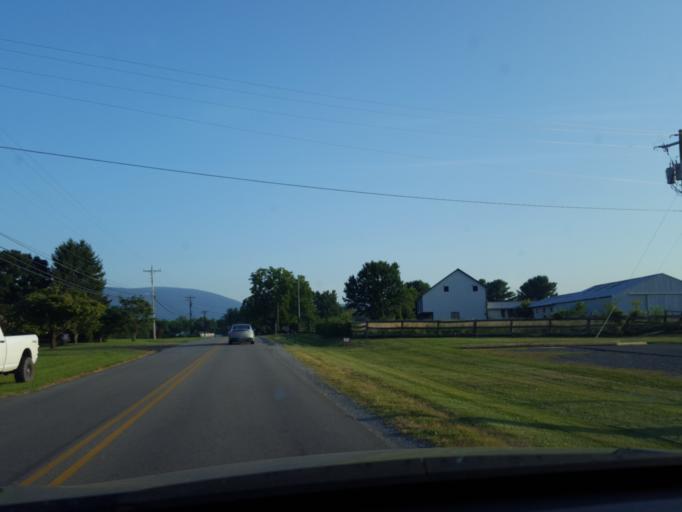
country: US
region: Virginia
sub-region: Augusta County
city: Lyndhurst
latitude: 38.0077
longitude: -78.9519
